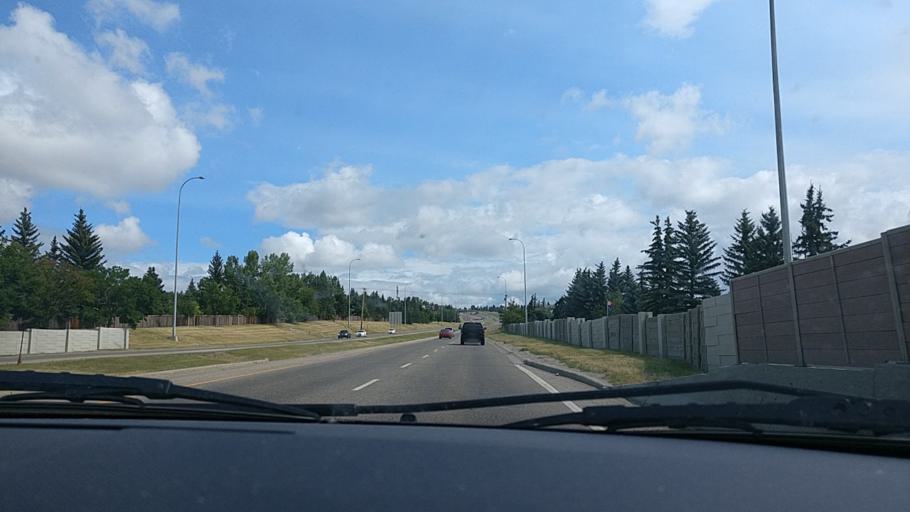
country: CA
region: Alberta
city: Calgary
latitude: 51.1147
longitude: -114.1737
